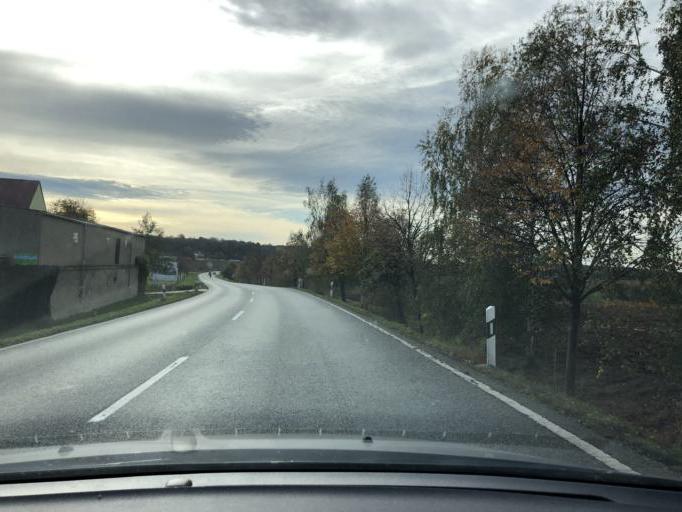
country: DE
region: Thuringia
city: Hirschfeld
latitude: 50.9759
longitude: 12.1341
